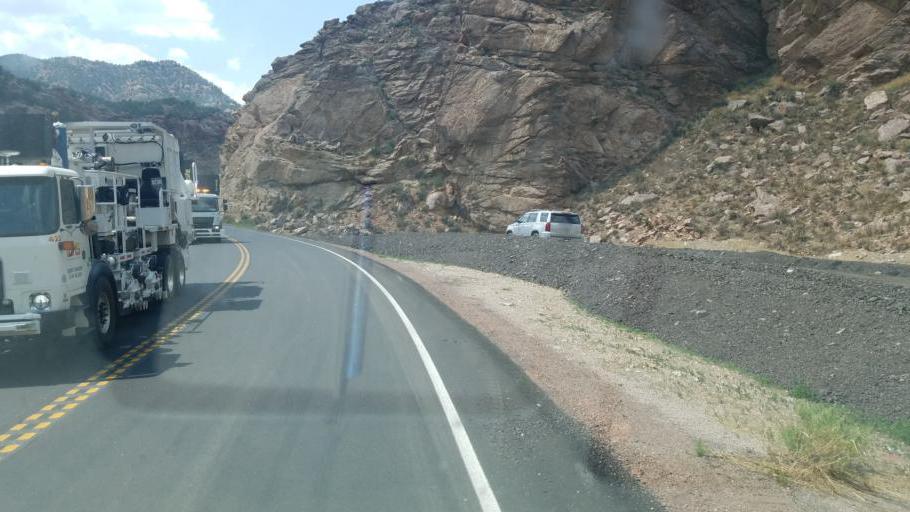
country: US
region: Colorado
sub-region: Fremont County
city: Canon City
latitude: 38.4381
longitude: -105.5392
